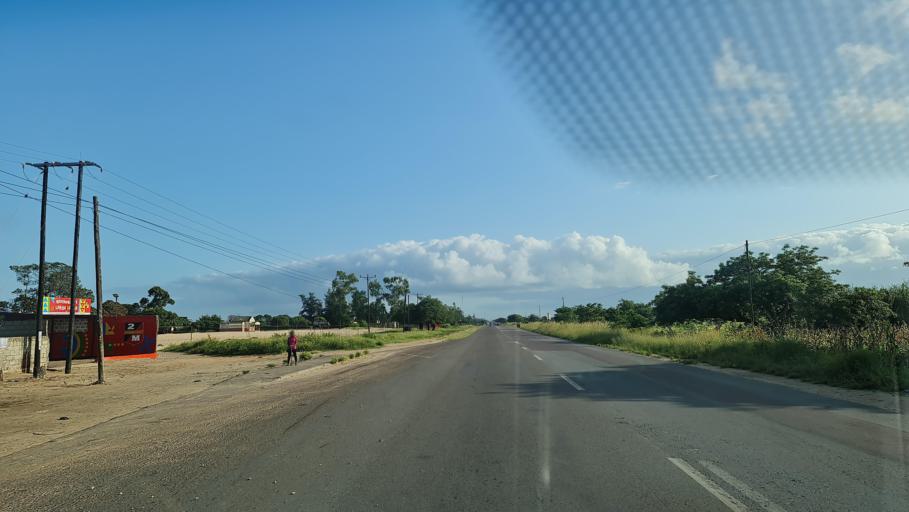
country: MZ
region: Maputo City
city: Maputo
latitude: -25.6825
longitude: 32.6660
